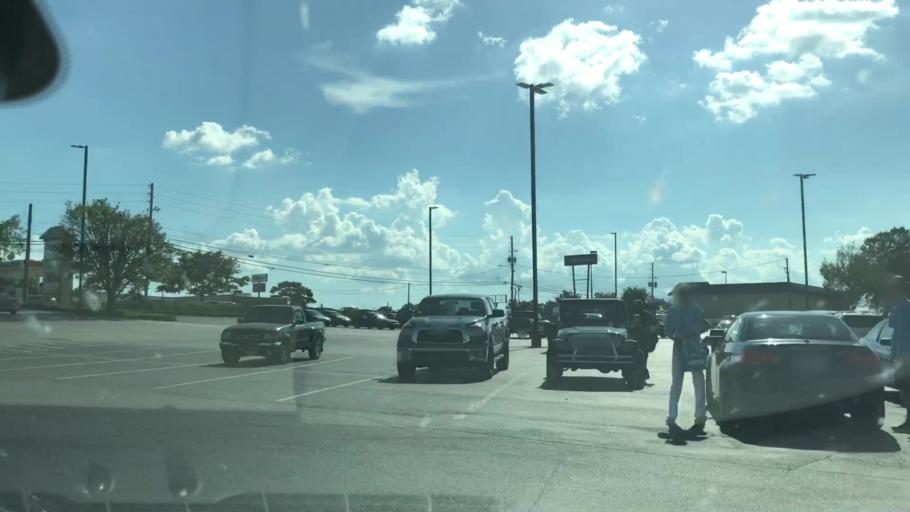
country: US
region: Georgia
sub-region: Troup County
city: La Grange
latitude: 33.0502
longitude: -85.0237
